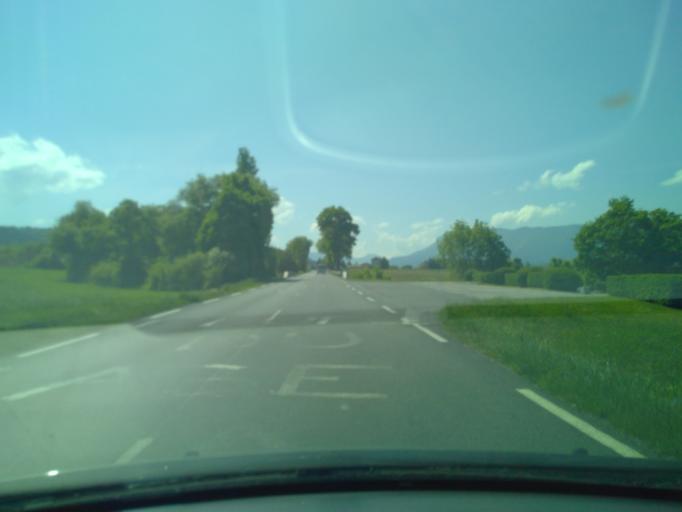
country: FR
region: Rhone-Alpes
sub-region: Departement de la Drome
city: Die
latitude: 44.7228
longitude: 5.3984
